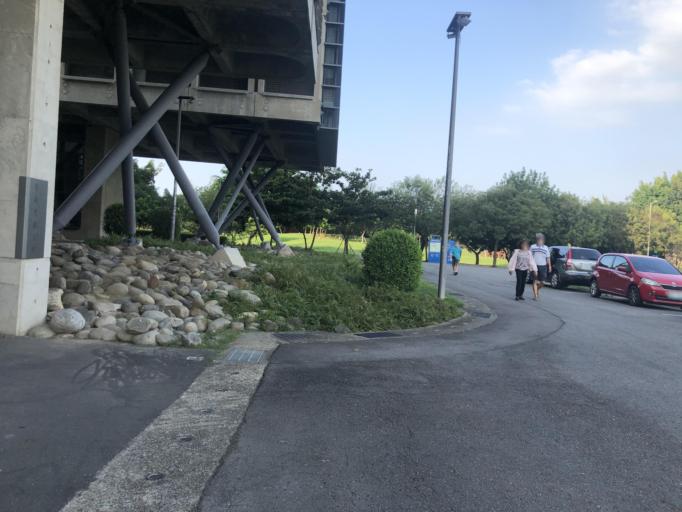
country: TW
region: Taiwan
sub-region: Tainan
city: Tainan
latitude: 23.0580
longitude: 120.2360
